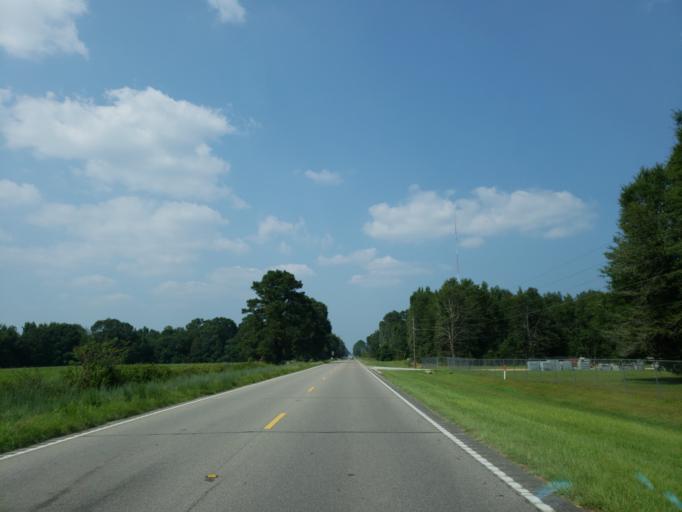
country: US
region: Mississippi
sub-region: Forrest County
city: Glendale
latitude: 31.4470
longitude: -89.2864
